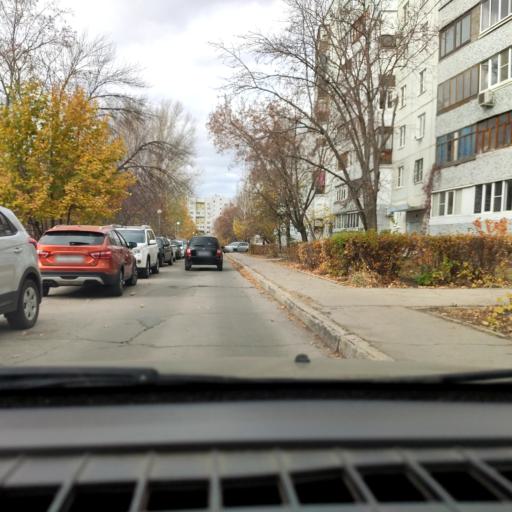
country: RU
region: Samara
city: Tol'yatti
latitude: 53.5313
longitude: 49.3351
